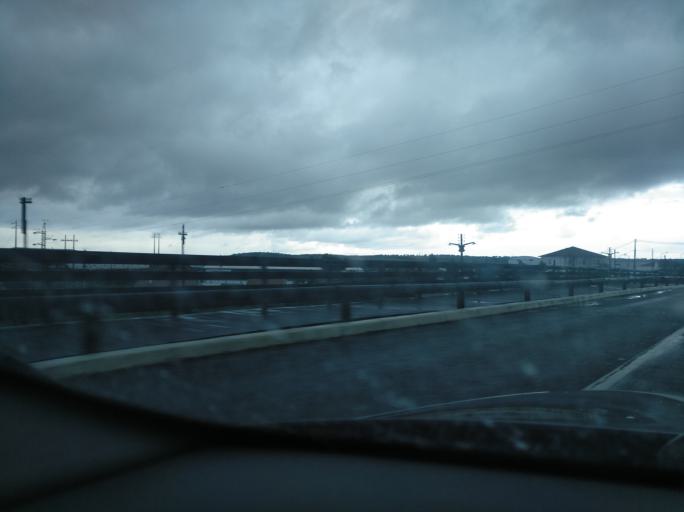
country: PT
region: Beja
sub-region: Aljustrel
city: Aljustrel
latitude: 37.8782
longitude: -8.1539
